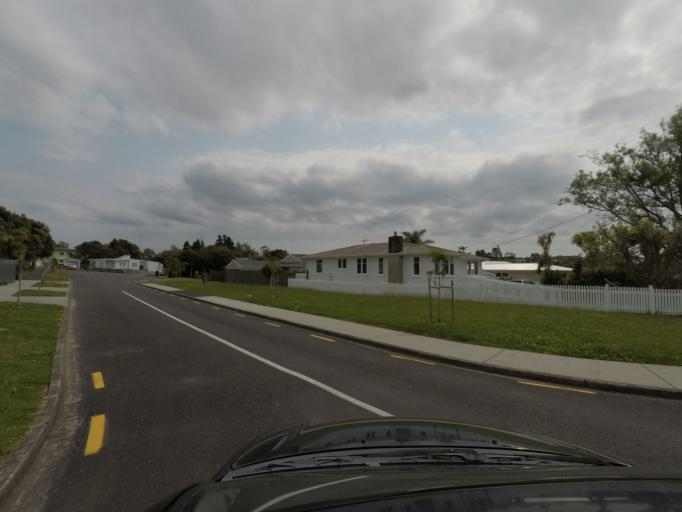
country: NZ
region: Auckland
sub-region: Auckland
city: Rosebank
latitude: -36.8354
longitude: 174.6416
